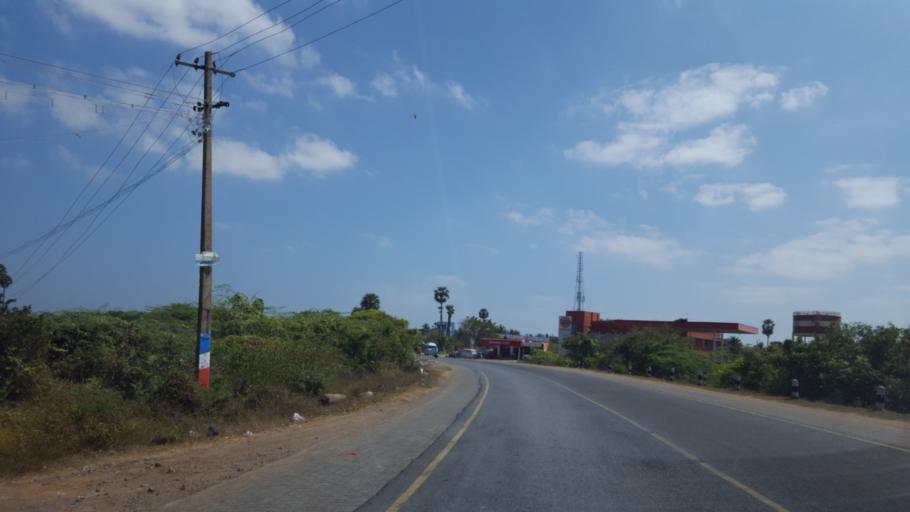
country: IN
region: Tamil Nadu
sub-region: Kancheepuram
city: Mamallapuram
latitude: 12.6149
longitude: 80.1721
